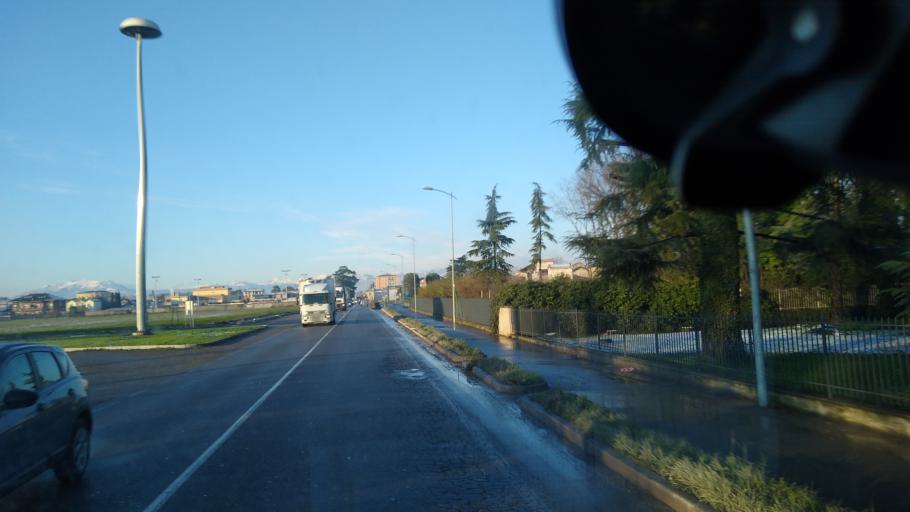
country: IT
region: Lombardy
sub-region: Provincia di Bergamo
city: Urgnano
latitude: 45.5932
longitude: 9.7013
